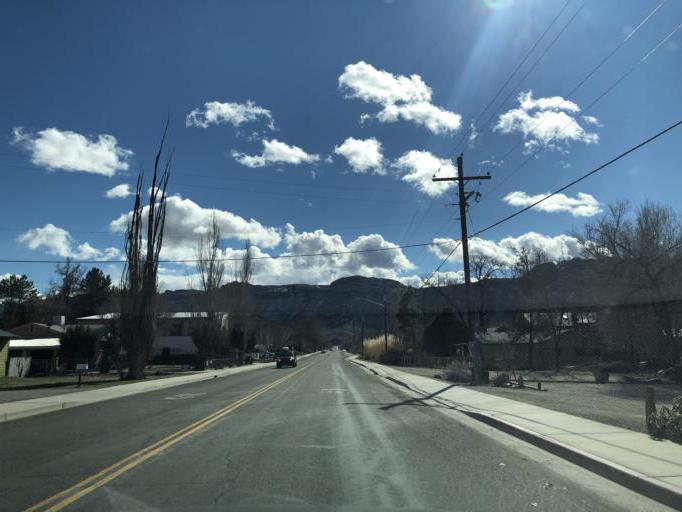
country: US
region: Utah
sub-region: Grand County
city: Moab
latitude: 38.5841
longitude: -109.5611
